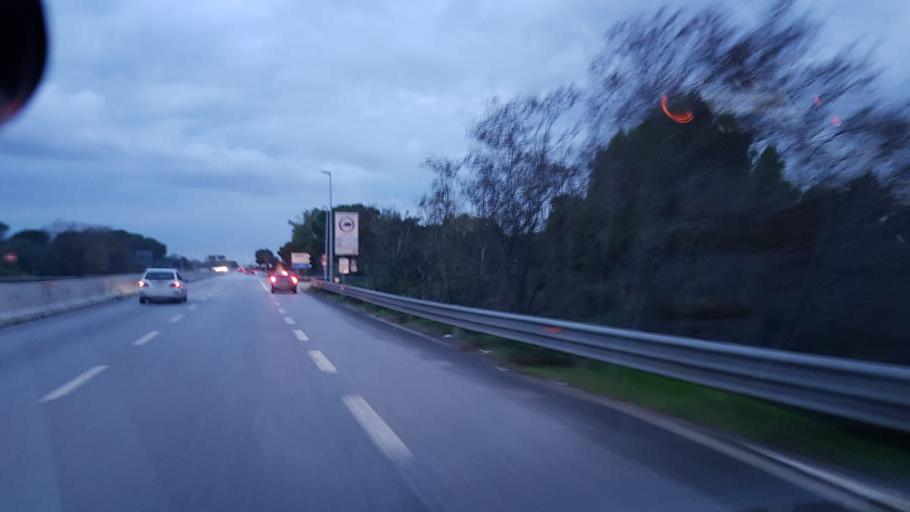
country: IT
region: Apulia
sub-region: Provincia di Taranto
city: Paolo VI
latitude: 40.5054
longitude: 17.2644
